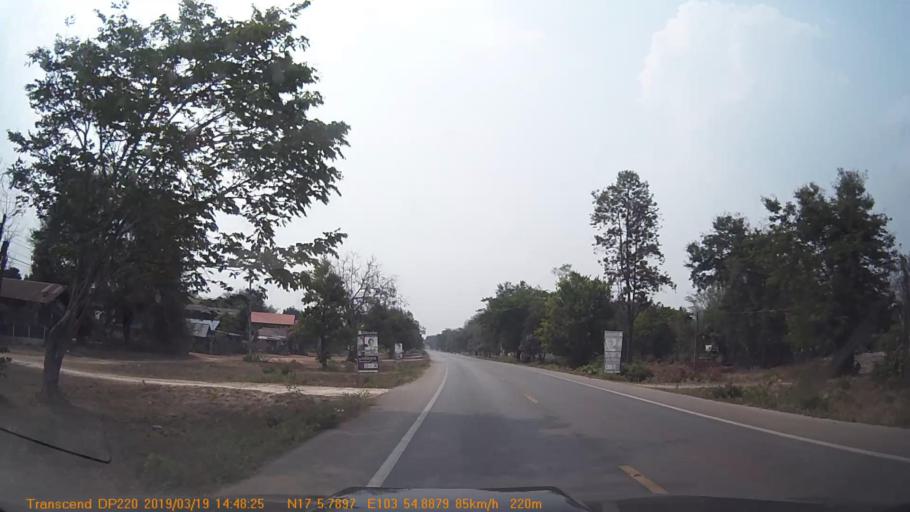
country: TH
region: Sakon Nakhon
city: Kut Bak
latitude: 17.0967
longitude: 103.9145
